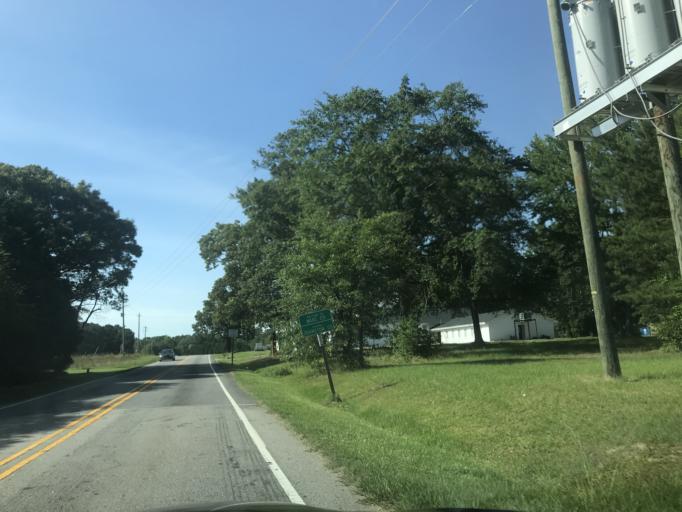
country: US
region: North Carolina
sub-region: Johnston County
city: Clayton
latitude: 35.6493
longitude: -78.5399
